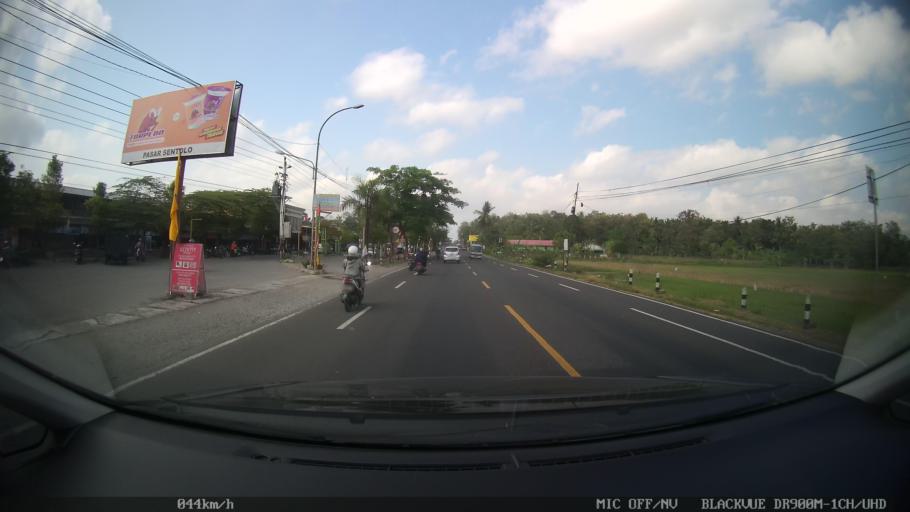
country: ID
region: Daerah Istimewa Yogyakarta
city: Srandakan
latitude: -7.8465
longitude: 110.2180
